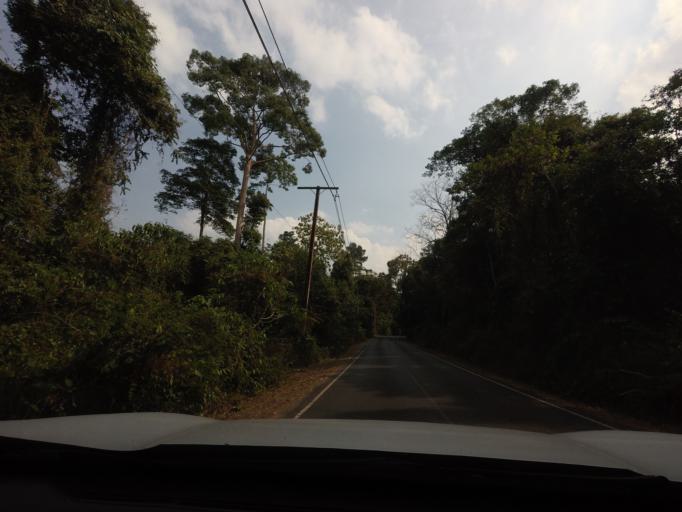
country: TH
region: Nakhon Ratchasima
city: Pak Chong
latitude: 14.4561
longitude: 101.3755
